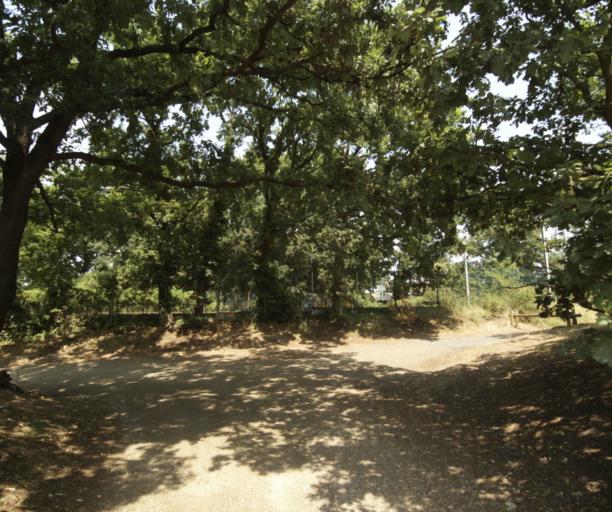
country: FR
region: Ile-de-France
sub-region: Departement des Yvelines
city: Conflans-Sainte-Honorine
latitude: 48.9993
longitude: 2.1174
